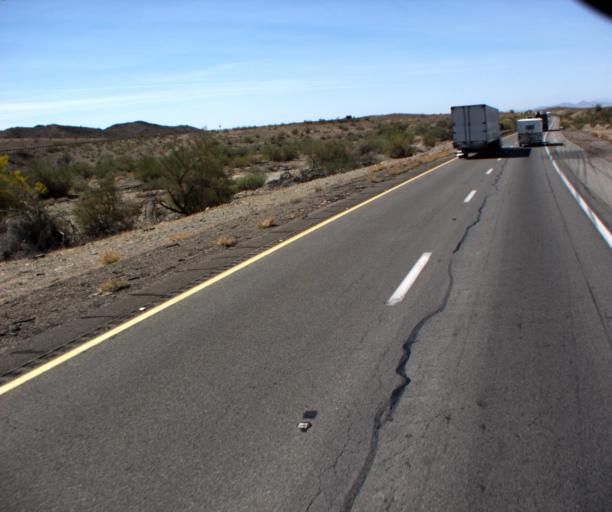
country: US
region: Arizona
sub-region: La Paz County
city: Ehrenberg
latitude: 33.6364
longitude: -114.3934
